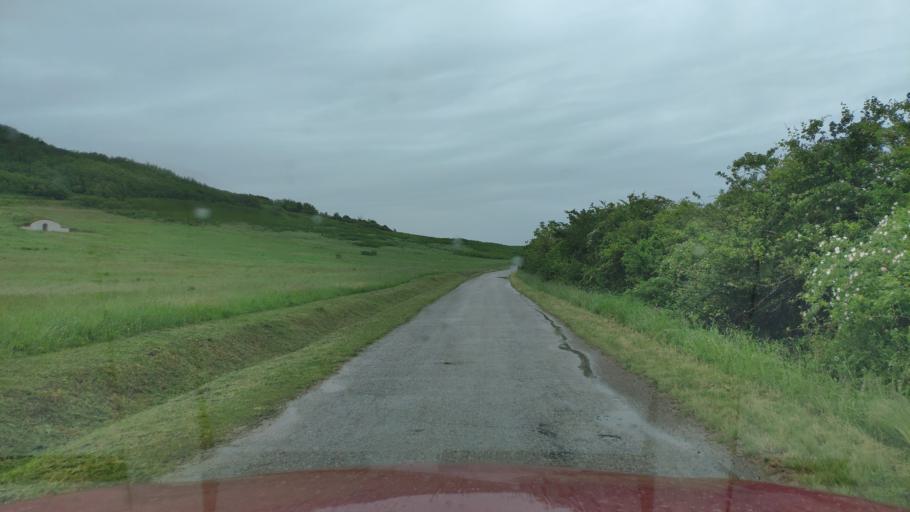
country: HU
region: Borsod-Abauj-Zemplen
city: Satoraljaujhely
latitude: 48.4301
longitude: 21.6964
